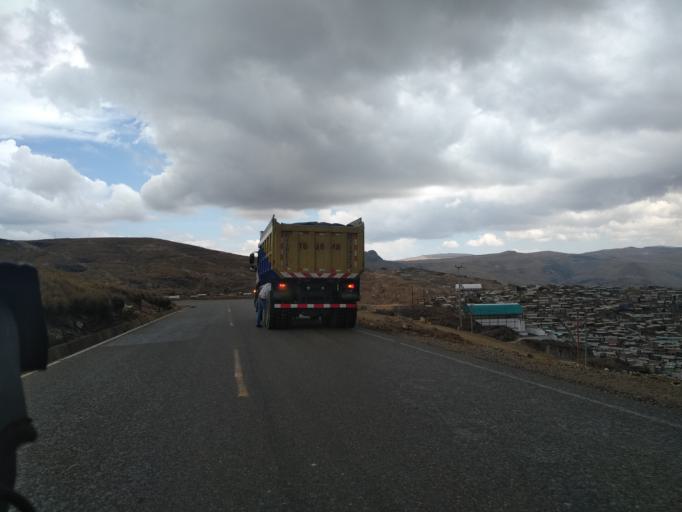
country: PE
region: La Libertad
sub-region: Provincia de Santiago de Chuco
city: Quiruvilca
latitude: -7.9966
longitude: -78.3099
